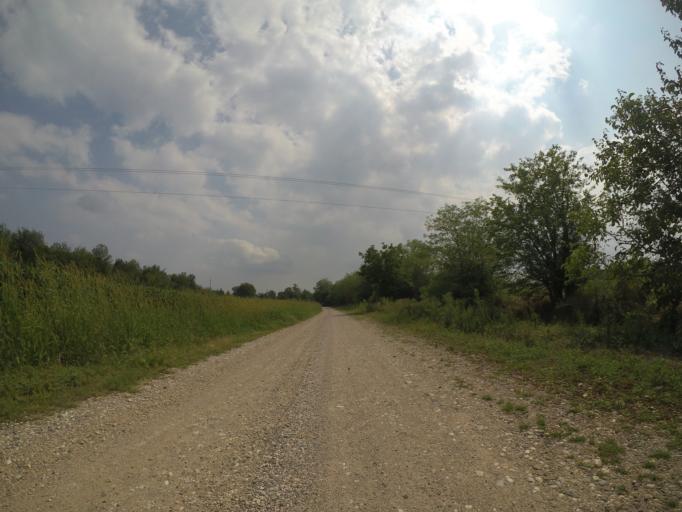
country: IT
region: Friuli Venezia Giulia
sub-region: Provincia di Udine
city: Codroipo
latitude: 45.9728
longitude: 13.0056
